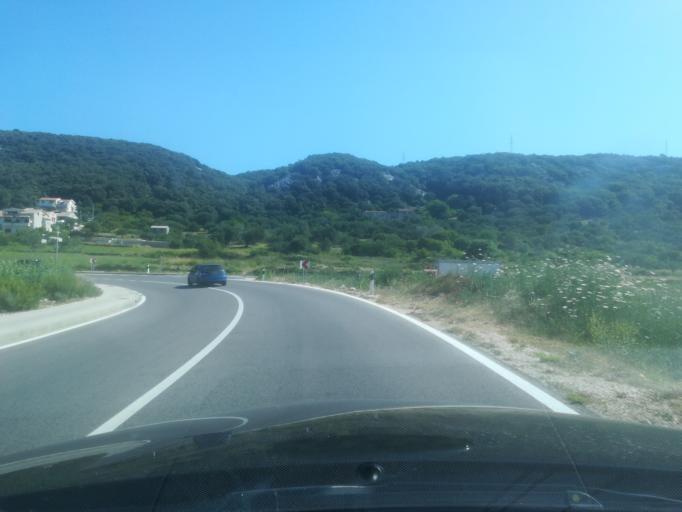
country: HR
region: Primorsko-Goranska
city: Supetarska Draga
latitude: 44.7967
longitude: 14.7337
